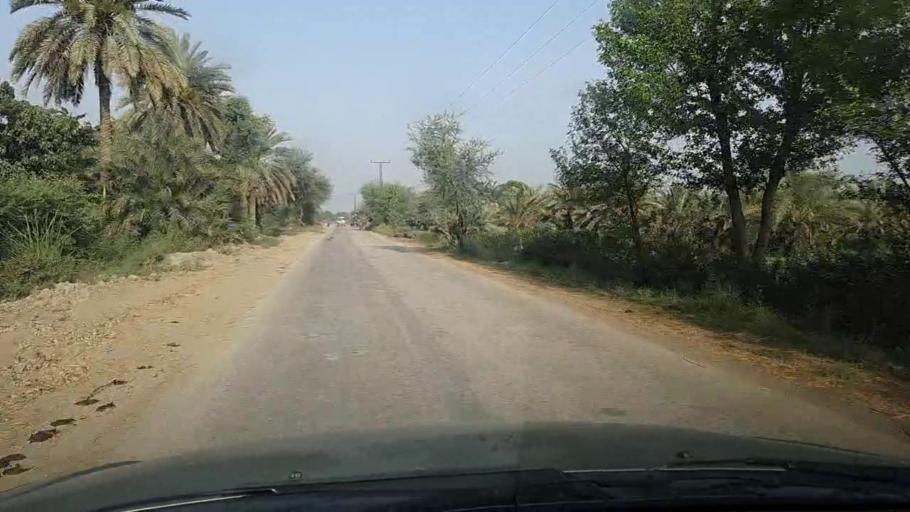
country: PK
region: Sindh
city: Pir jo Goth
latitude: 27.5717
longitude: 68.5985
